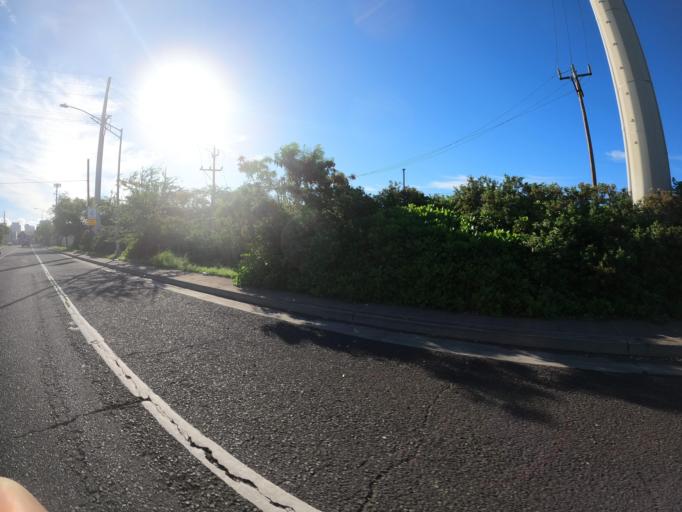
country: US
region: Hawaii
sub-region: Honolulu County
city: Honolulu
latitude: 21.3066
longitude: -157.8790
